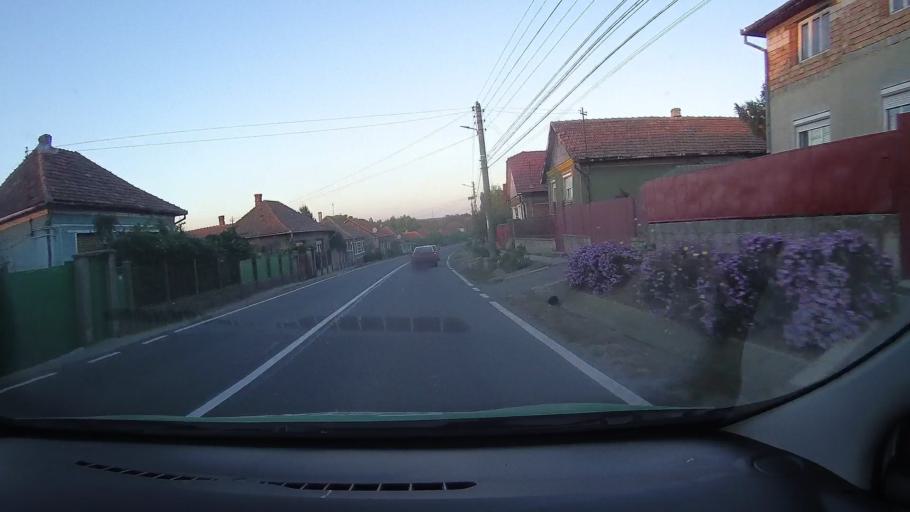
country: RO
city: Szekelyhid
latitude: 47.3548
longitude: 22.1093
